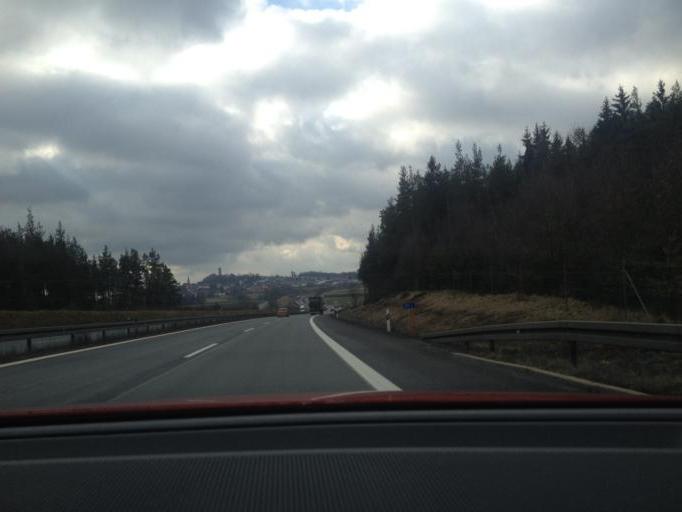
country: DE
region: Bavaria
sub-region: Upper Franconia
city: Thierstein
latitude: 50.1244
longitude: 12.0937
